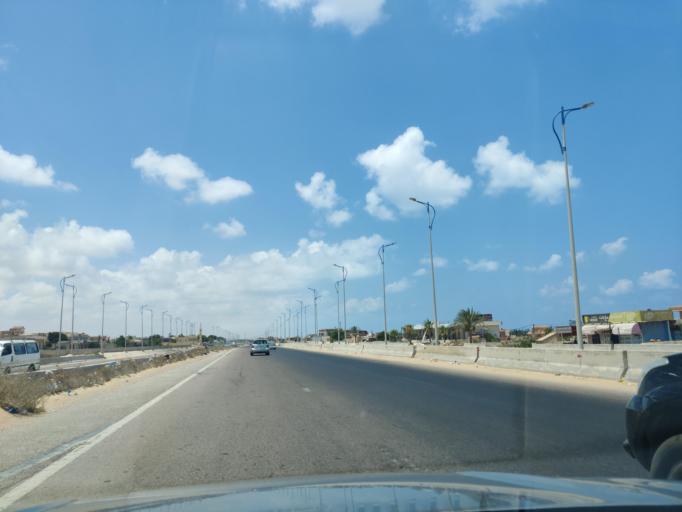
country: EG
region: Alexandria
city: Alexandria
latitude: 30.9618
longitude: 29.5458
